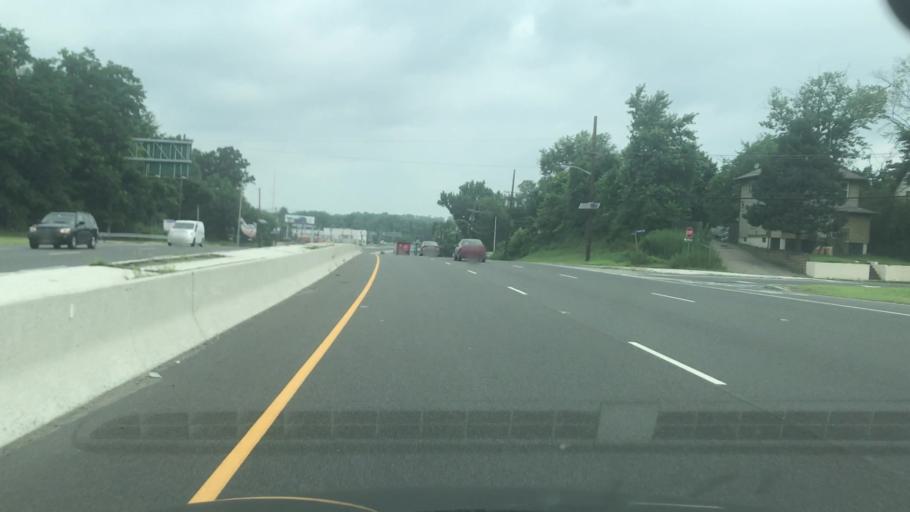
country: US
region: New Jersey
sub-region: Passaic County
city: Wayne
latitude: 40.9174
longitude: -74.2661
